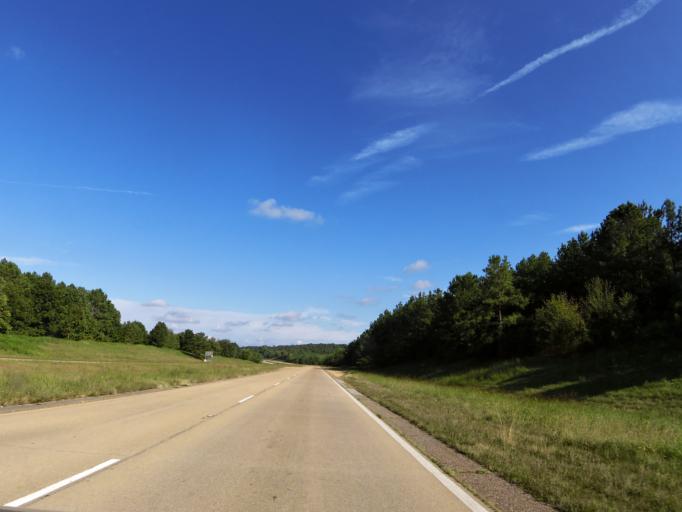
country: US
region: Mississippi
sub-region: Tishomingo County
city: Iuka
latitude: 34.7741
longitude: -88.1482
